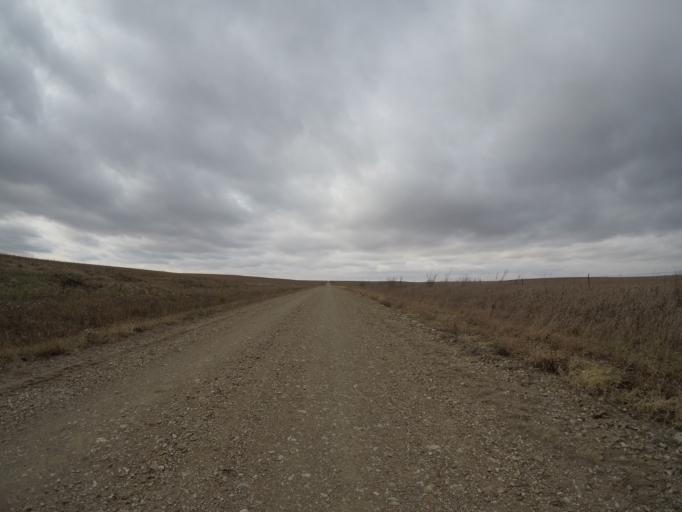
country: US
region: Kansas
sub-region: Morris County
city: Council Grove
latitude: 38.7245
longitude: -96.1940
